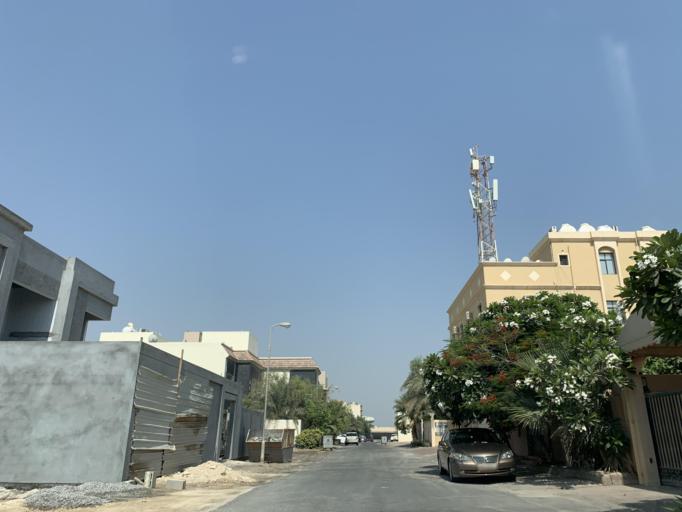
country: BH
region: Northern
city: Madinat `Isa
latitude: 26.1959
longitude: 50.5103
